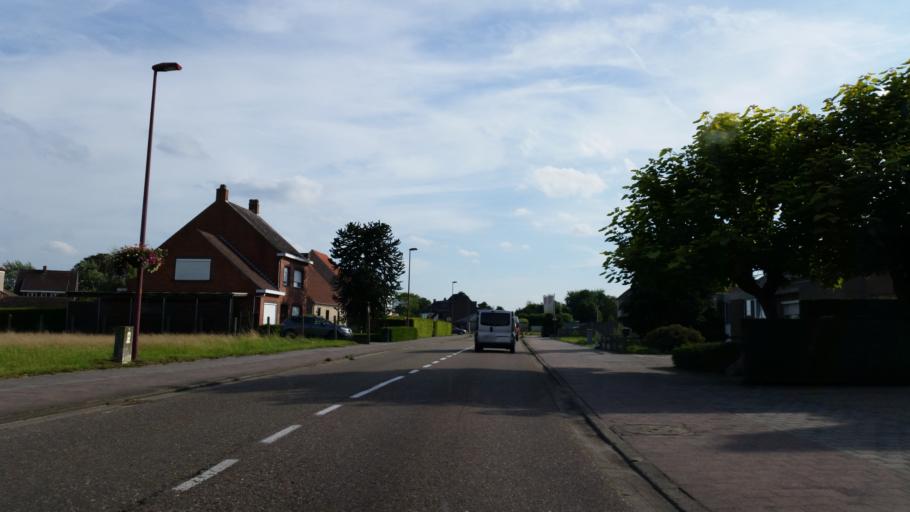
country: BE
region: Flanders
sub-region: Provincie Antwerpen
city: Olen
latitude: 51.1370
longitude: 4.9045
